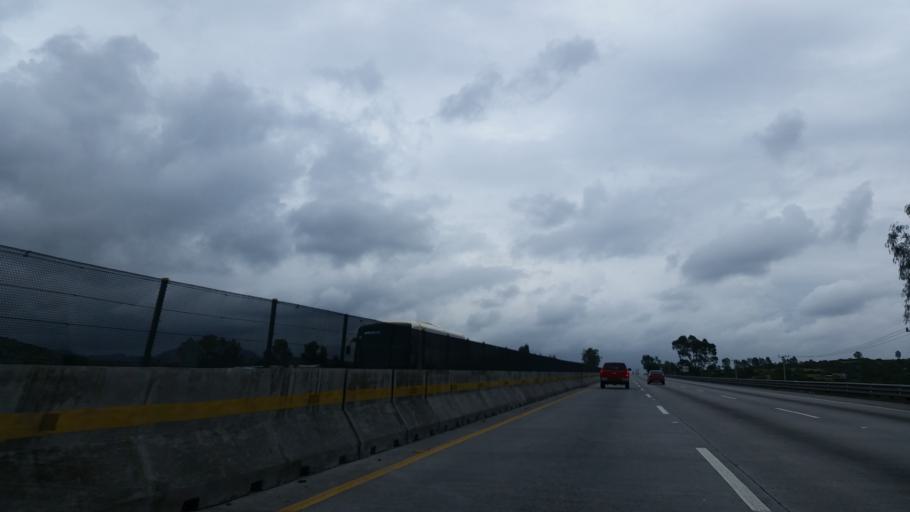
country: MX
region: Hidalgo
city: Tepeji de Ocampo
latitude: 19.9223
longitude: -99.3718
